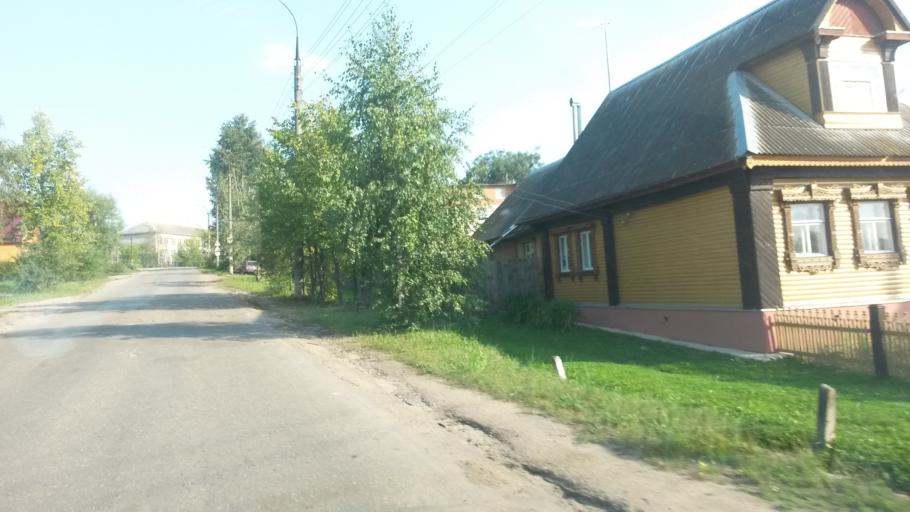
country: RU
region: Jaroslavl
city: Petrovsk
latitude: 57.0104
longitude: 39.2664
